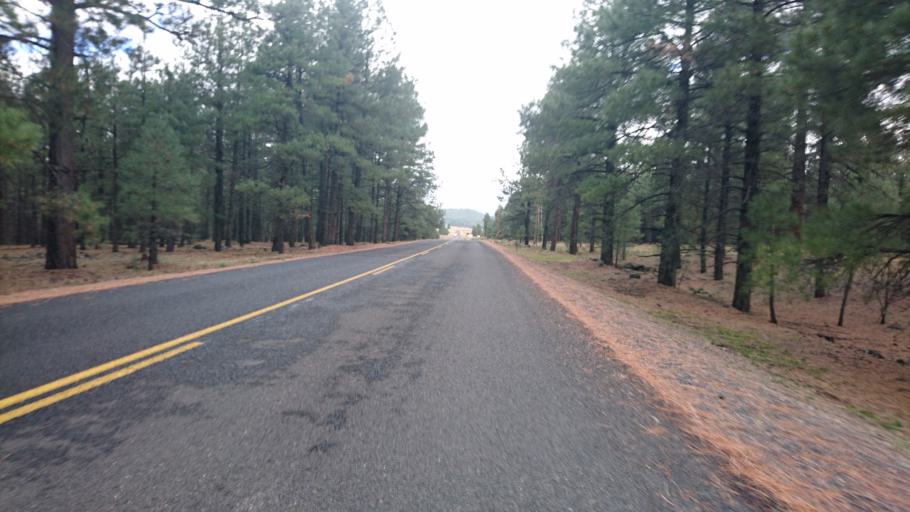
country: US
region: Arizona
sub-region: Coconino County
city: Parks
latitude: 35.2628
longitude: -111.8738
